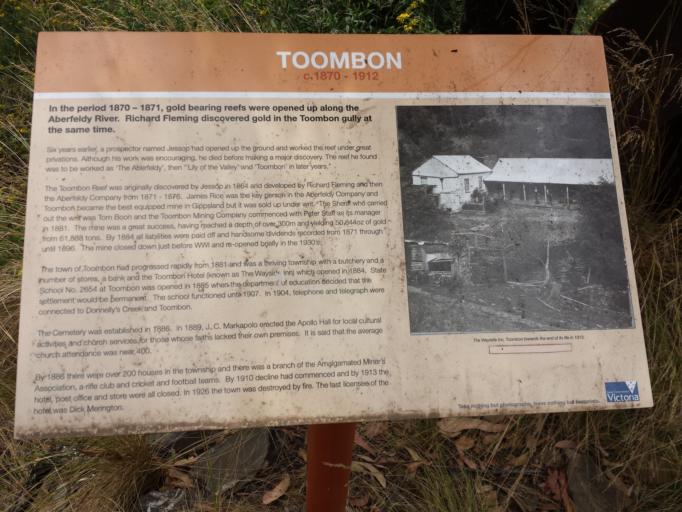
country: AU
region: Victoria
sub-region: Wellington
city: Heyfield
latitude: -37.7351
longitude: 146.4045
